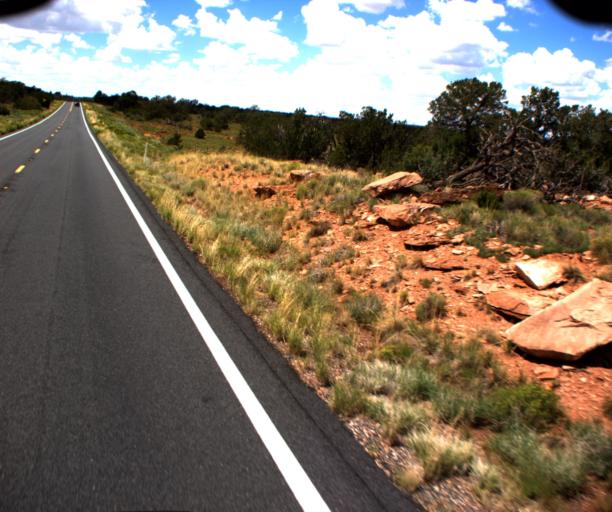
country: US
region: Arizona
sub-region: Coconino County
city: Parks
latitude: 35.6012
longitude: -112.0282
